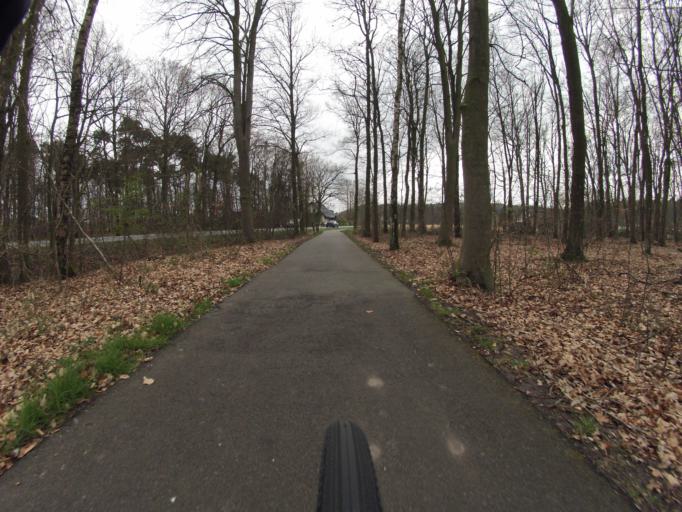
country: DE
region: North Rhine-Westphalia
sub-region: Regierungsbezirk Munster
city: Recke
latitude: 52.3396
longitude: 7.7180
